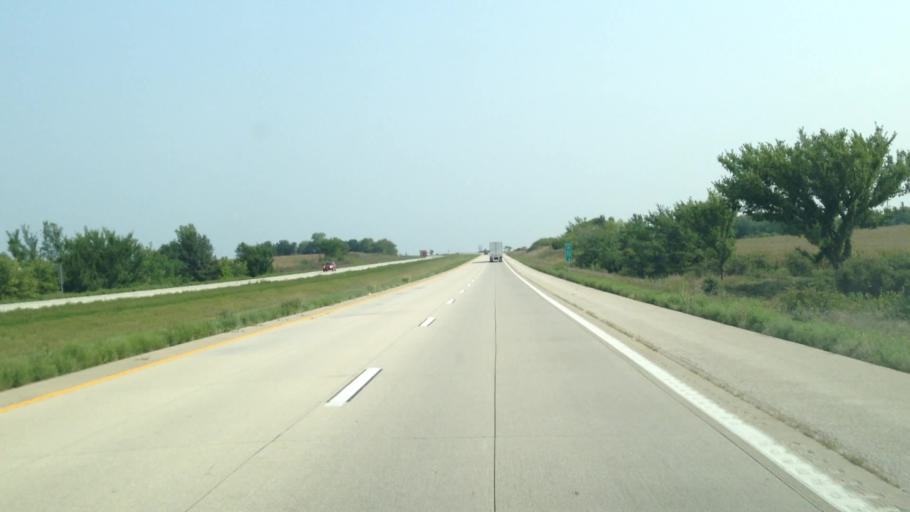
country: US
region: Missouri
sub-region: Daviess County
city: Gallatin
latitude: 39.9690
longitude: -94.0974
